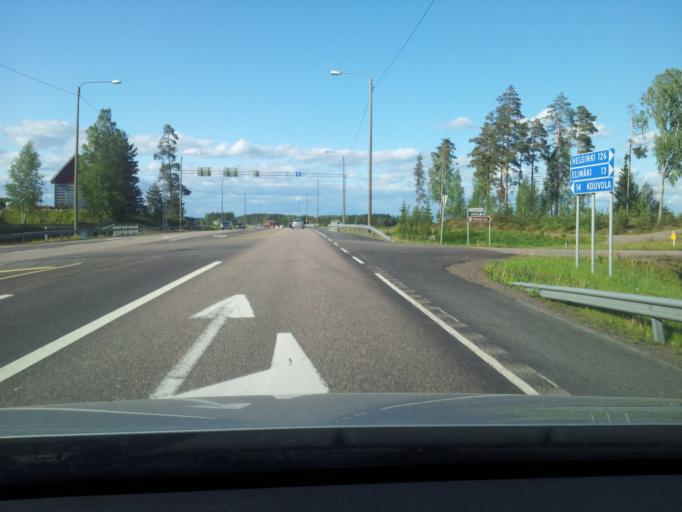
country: FI
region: Kymenlaakso
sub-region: Kouvola
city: Elimaeki
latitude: 60.8164
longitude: 26.5268
